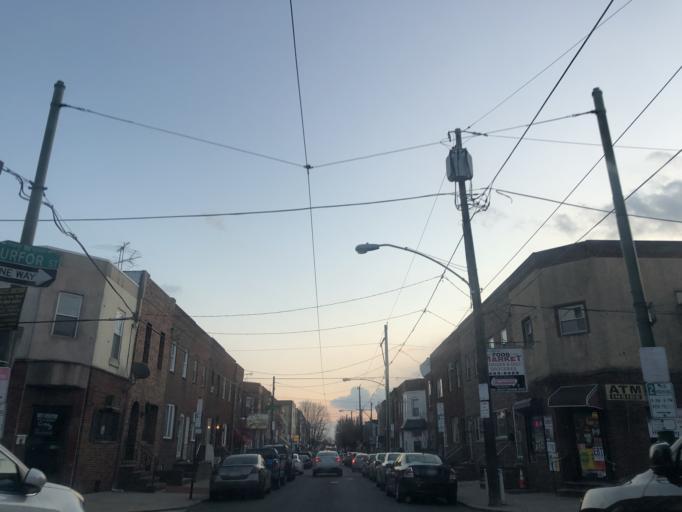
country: US
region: Pennsylvania
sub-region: Philadelphia County
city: Philadelphia
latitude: 39.9211
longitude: -75.1666
